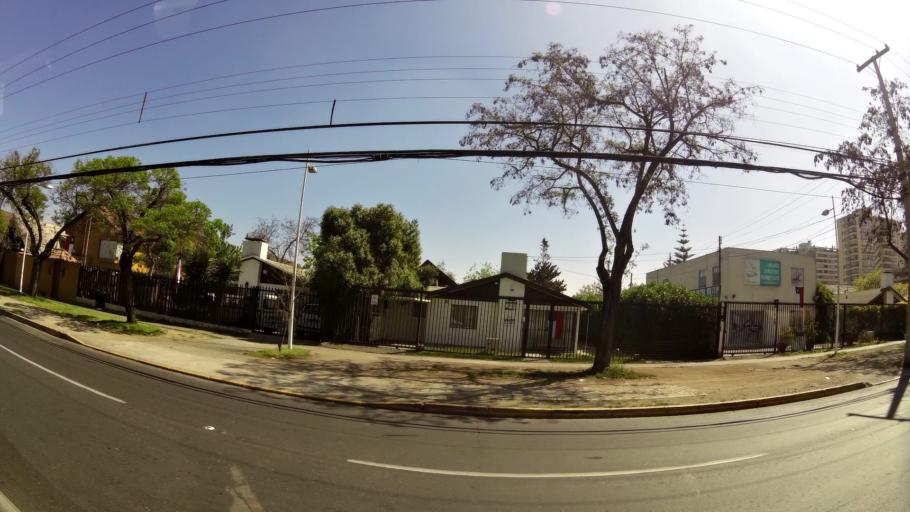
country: CL
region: Santiago Metropolitan
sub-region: Provincia de Santiago
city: Villa Presidente Frei, Nunoa, Santiago, Chile
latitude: -33.4212
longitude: -70.5534
